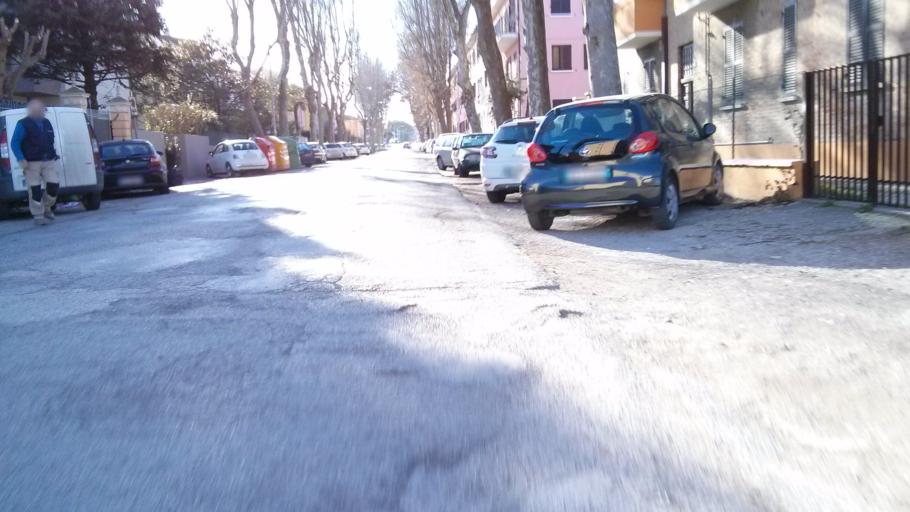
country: IT
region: The Marches
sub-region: Provincia di Pesaro e Urbino
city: Fano
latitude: 43.8380
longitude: 13.0321
